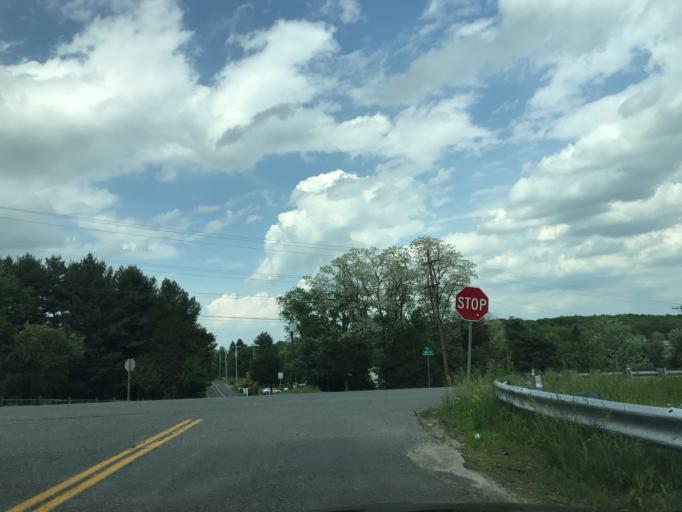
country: US
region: Pennsylvania
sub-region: York County
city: Susquehanna Trails
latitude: 39.7016
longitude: -76.3338
